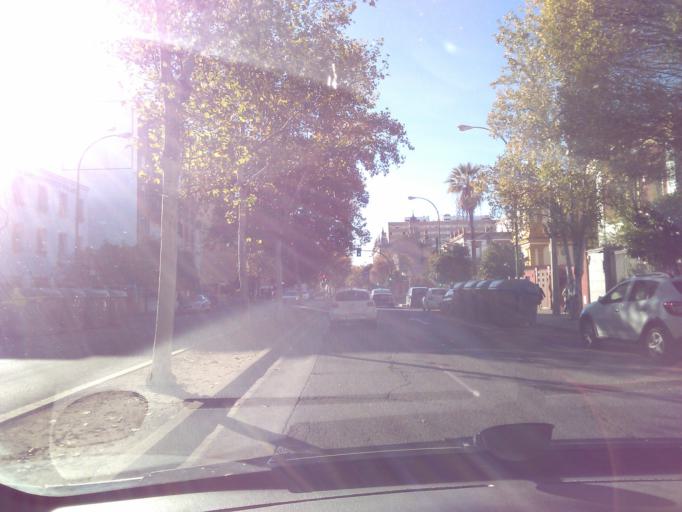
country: ES
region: Andalusia
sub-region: Provincia de Sevilla
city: Sevilla
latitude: 37.3852
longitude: -5.9654
